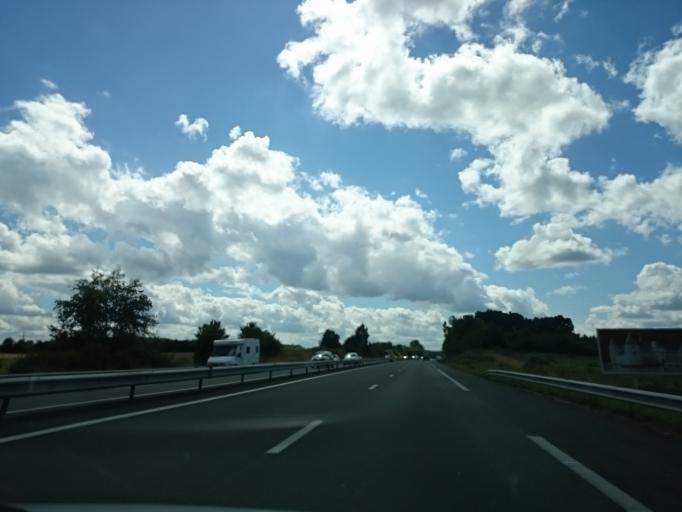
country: FR
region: Pays de la Loire
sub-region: Departement de Maine-et-Loire
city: Seiches-sur-le-Loir
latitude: 47.5974
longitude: -0.3128
